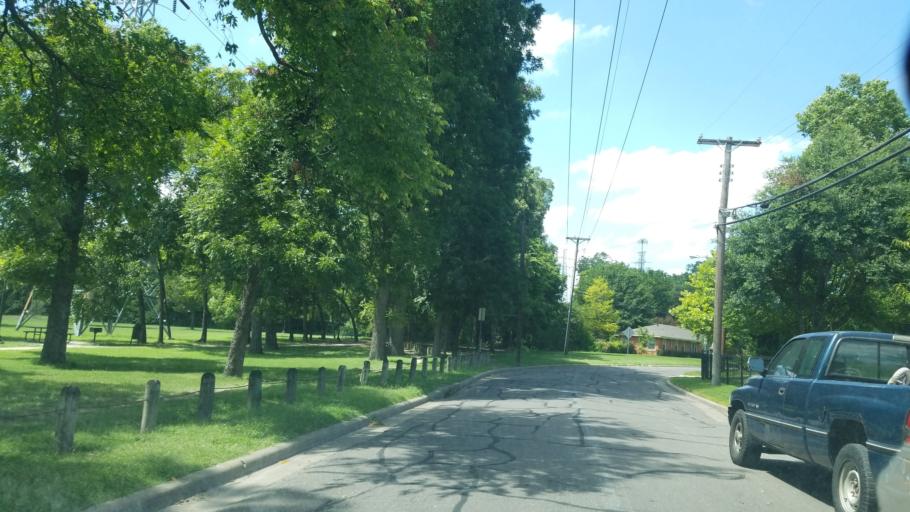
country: US
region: Texas
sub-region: Dallas County
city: Balch Springs
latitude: 32.7581
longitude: -96.7000
